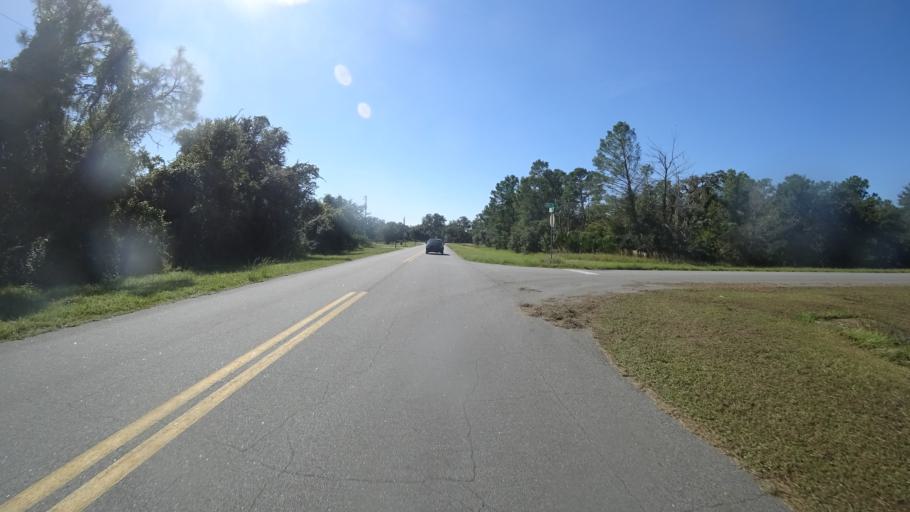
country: US
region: Florida
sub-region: Sarasota County
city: Lake Sarasota
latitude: 27.3519
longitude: -82.2464
